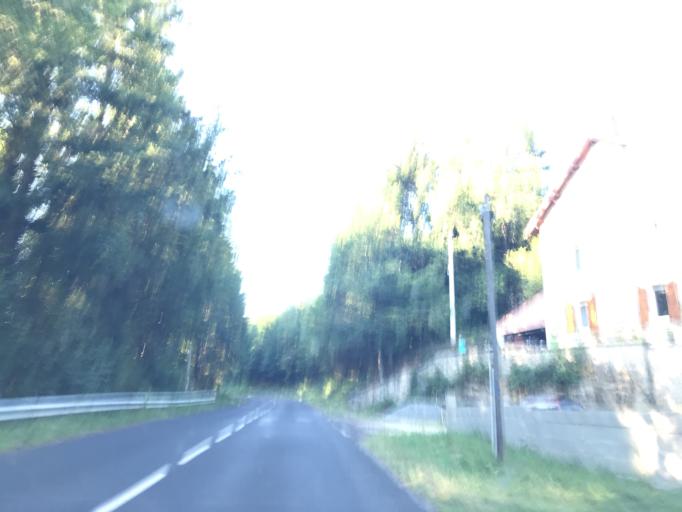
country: FR
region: Auvergne
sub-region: Departement du Puy-de-Dome
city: La Monnerie-le-Montel
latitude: 45.8767
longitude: 3.5993
